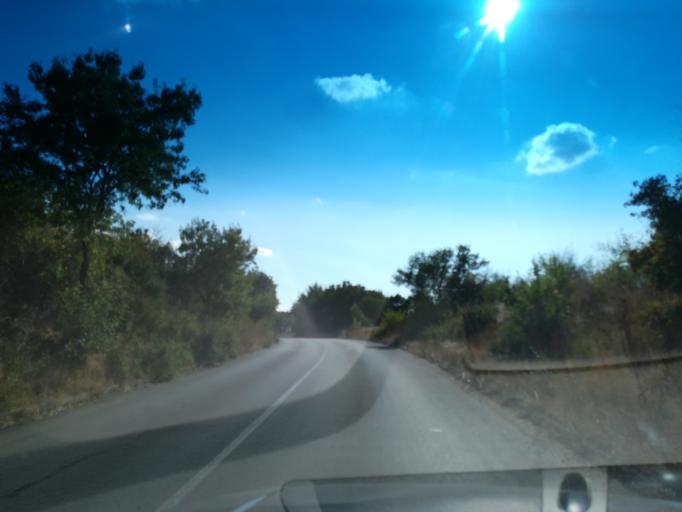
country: BG
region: Khaskovo
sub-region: Obshtina Mineralni Bani
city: Mineralni Bani
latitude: 42.0047
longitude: 25.3821
